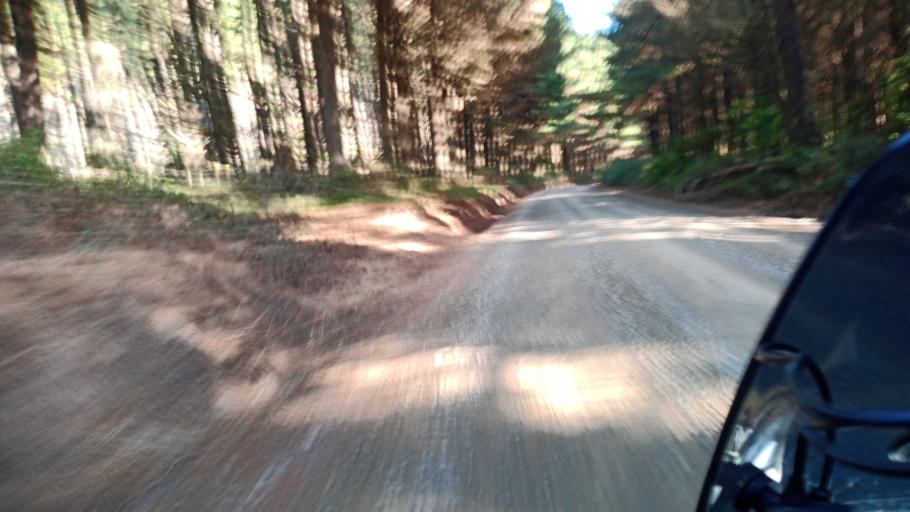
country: NZ
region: Hawke's Bay
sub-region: Wairoa District
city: Wairoa
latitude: -38.9331
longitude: 177.2368
